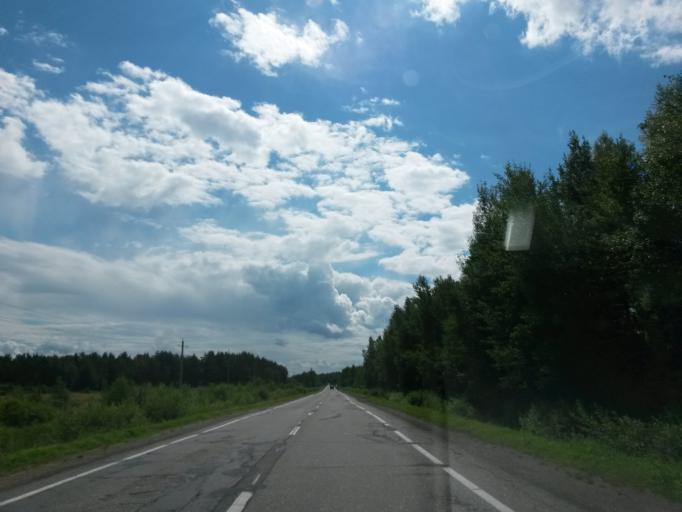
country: RU
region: Jaroslavl
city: Gavrilov-Yam
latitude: 57.2998
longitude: 39.9486
